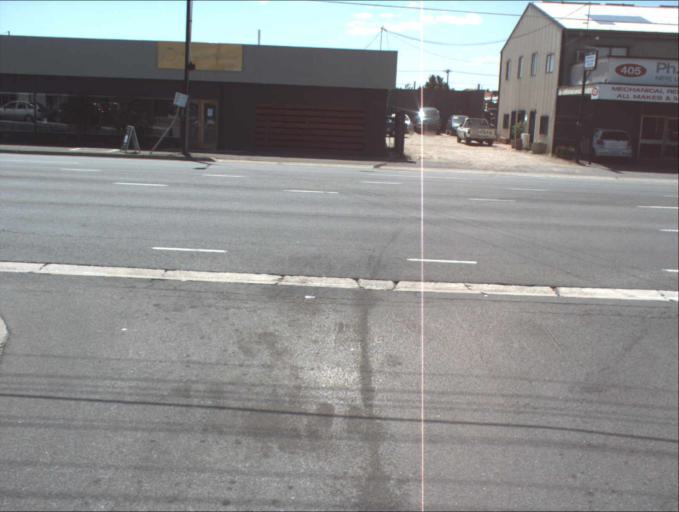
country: AU
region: South Australia
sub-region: Charles Sturt
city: Woodville North
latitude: -34.8507
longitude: 138.5490
